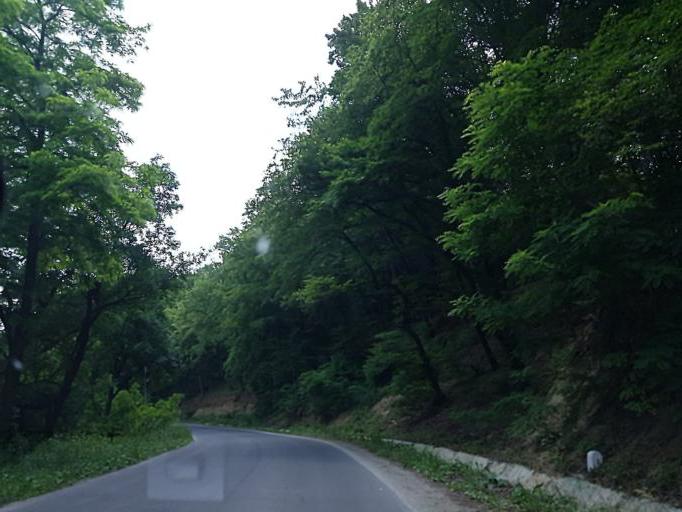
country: RO
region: Sibiu
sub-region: Comuna Seica Mare
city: Seica Mare
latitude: 46.0396
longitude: 24.1588
